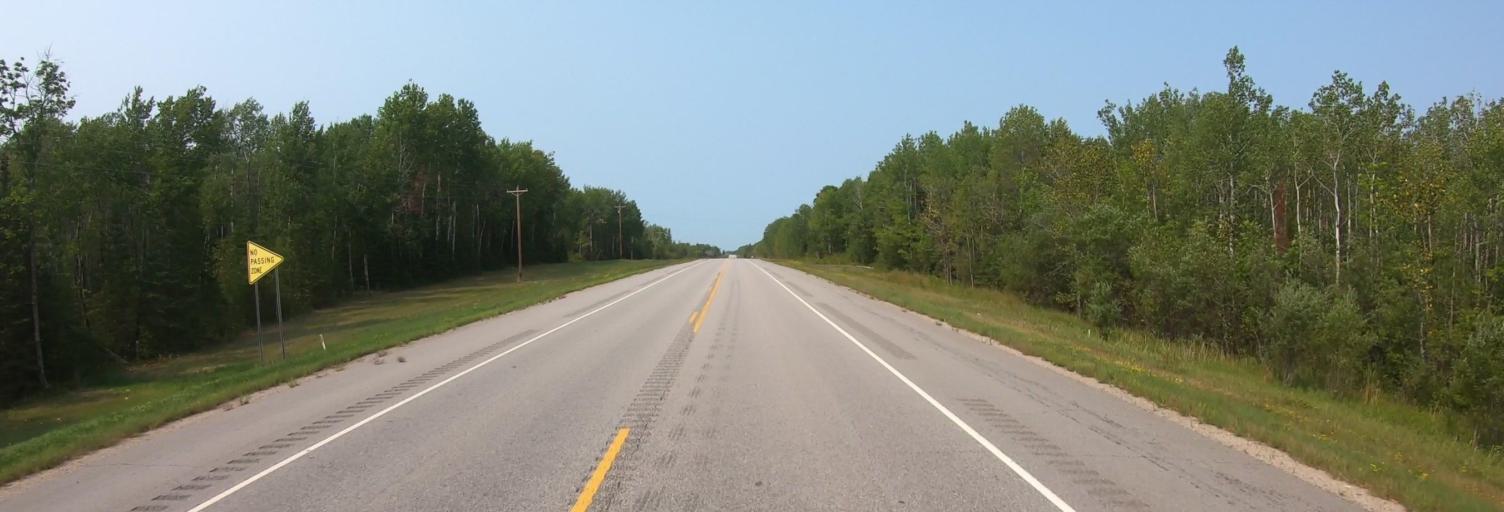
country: CA
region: Ontario
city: Fort Frances
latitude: 48.4091
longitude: -93.0948
